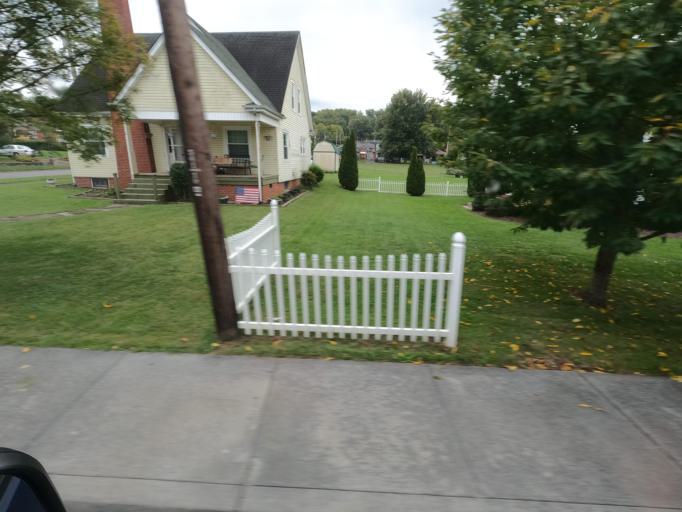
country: US
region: Tennessee
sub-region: Carter County
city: Elizabethton
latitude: 36.3453
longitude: -82.2282
